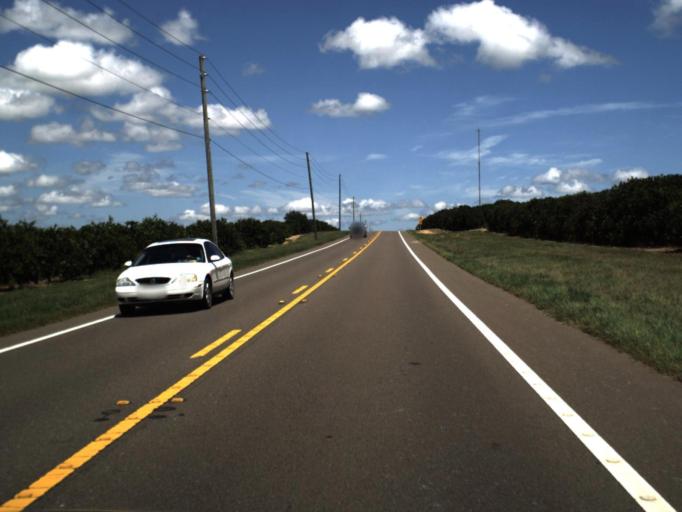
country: US
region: Florida
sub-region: Polk County
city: Babson Park
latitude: 27.8077
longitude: -81.5390
